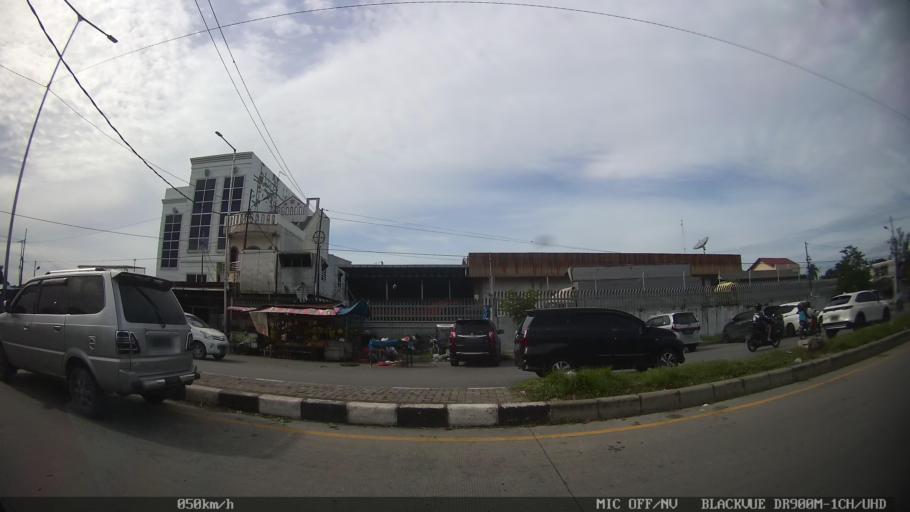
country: ID
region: North Sumatra
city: Medan
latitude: 3.6292
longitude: 98.6930
